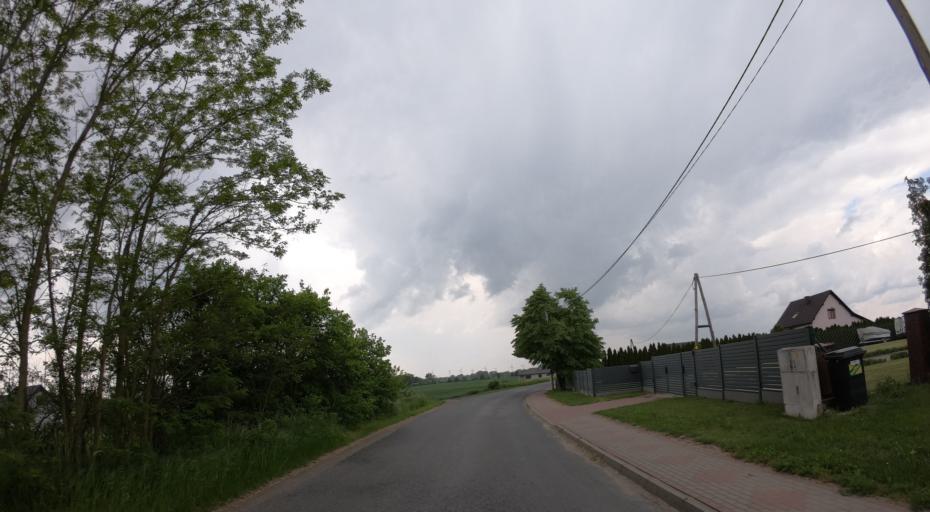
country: PL
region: West Pomeranian Voivodeship
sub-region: Powiat pyrzycki
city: Bielice
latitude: 53.2322
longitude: 14.7633
